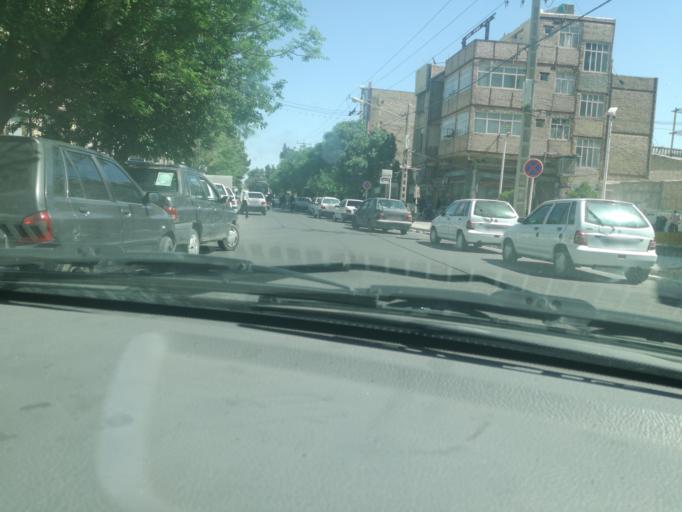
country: IR
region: Razavi Khorasan
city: Sarakhs
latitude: 36.5352
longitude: 61.1630
